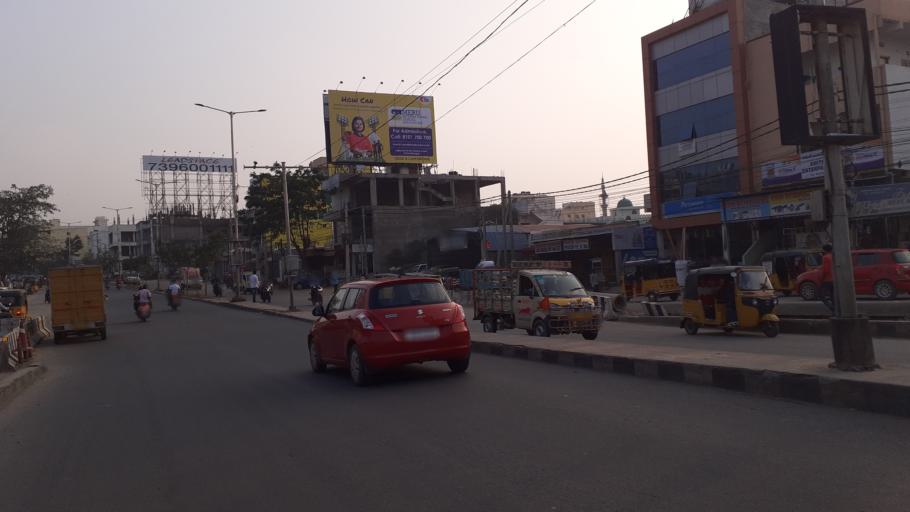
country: IN
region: Telangana
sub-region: Rangareddi
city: Kukatpalli
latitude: 17.4806
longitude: 78.3610
